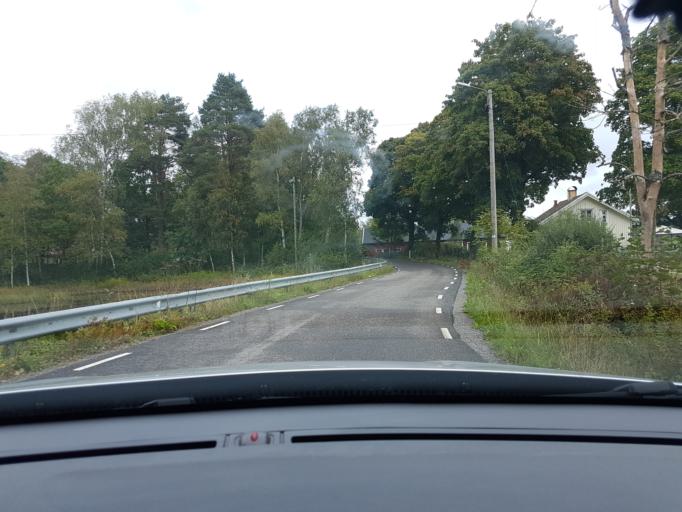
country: SE
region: Vaestra Goetaland
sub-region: Ale Kommun
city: Skepplanda
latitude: 57.8916
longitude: 12.1939
